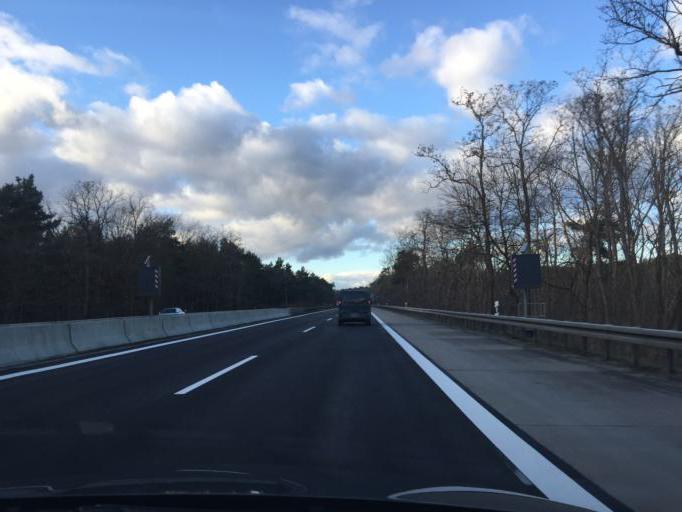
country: DE
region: Brandenburg
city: Lubbenau
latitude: 51.8210
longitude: 14.0125
